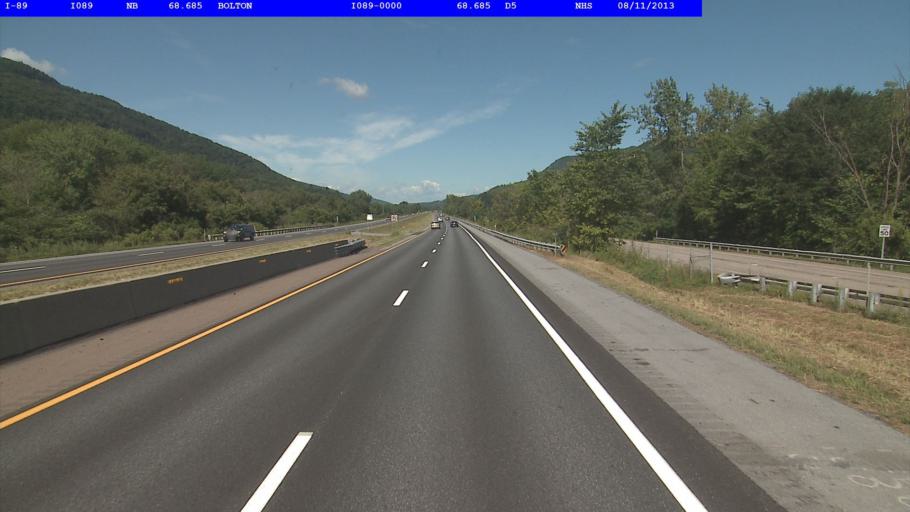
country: US
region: Vermont
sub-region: Washington County
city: Waterbury
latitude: 44.3633
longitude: -72.8432
